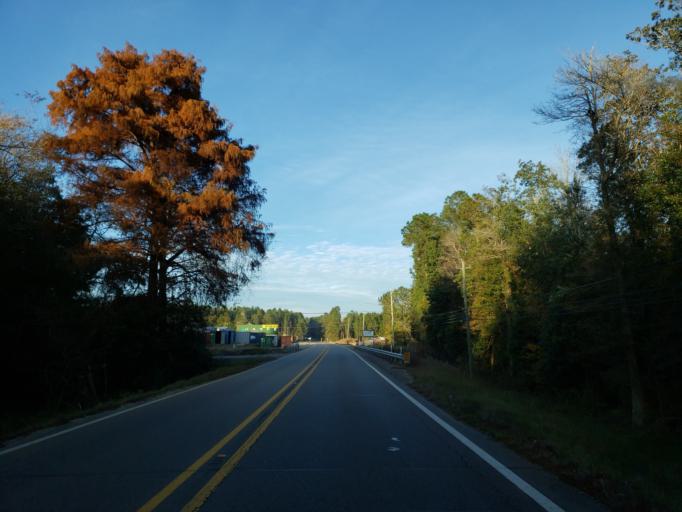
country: US
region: Mississippi
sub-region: Lamar County
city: Purvis
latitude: 31.1494
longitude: -89.4008
